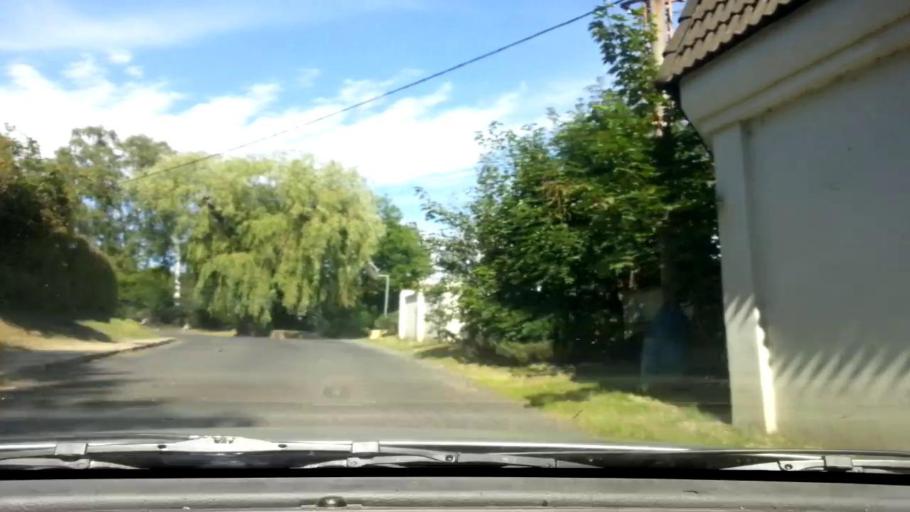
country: CZ
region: Karlovarsky
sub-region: Okres Cheb
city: Cheb
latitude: 50.0599
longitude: 12.3714
